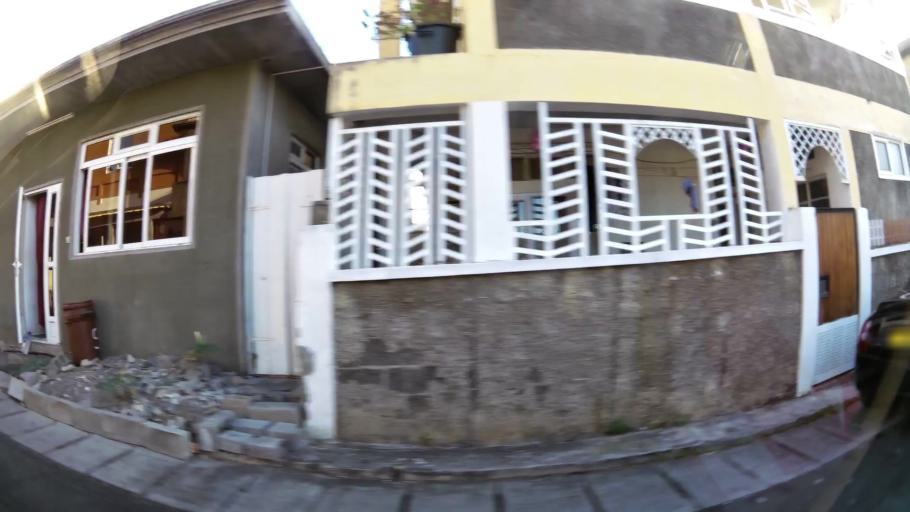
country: MU
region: Port Louis
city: Port Louis
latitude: -20.1743
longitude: 57.5098
